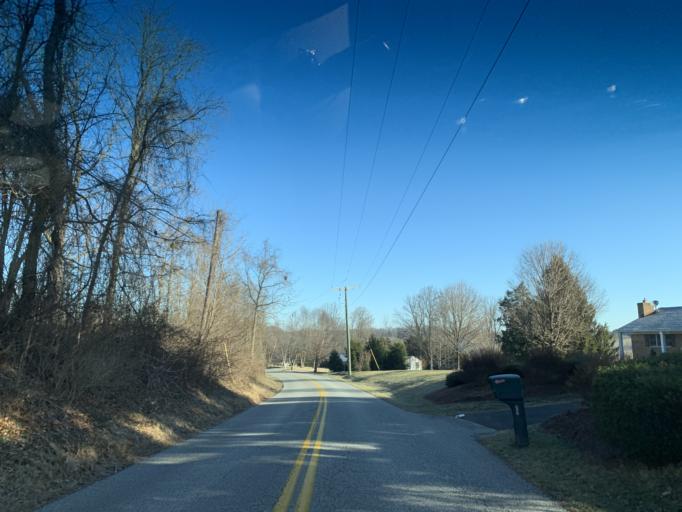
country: US
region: Maryland
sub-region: Harford County
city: Aberdeen
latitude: 39.5839
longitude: -76.2331
